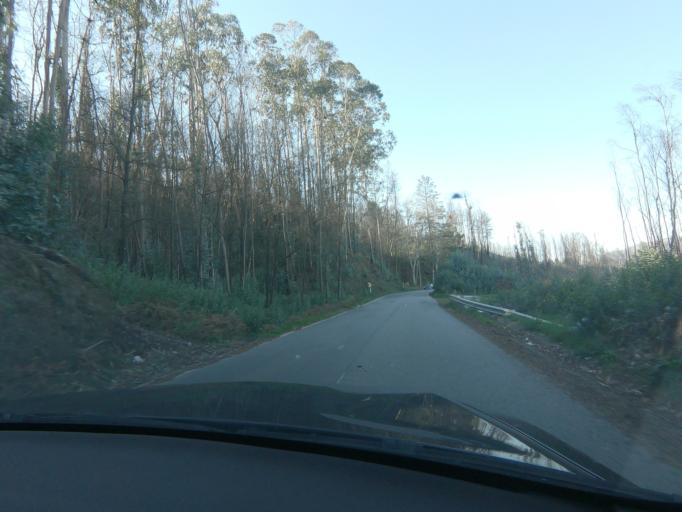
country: PT
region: Viseu
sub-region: Vouzela
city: Vouzela
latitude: 40.7269
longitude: -8.1330
